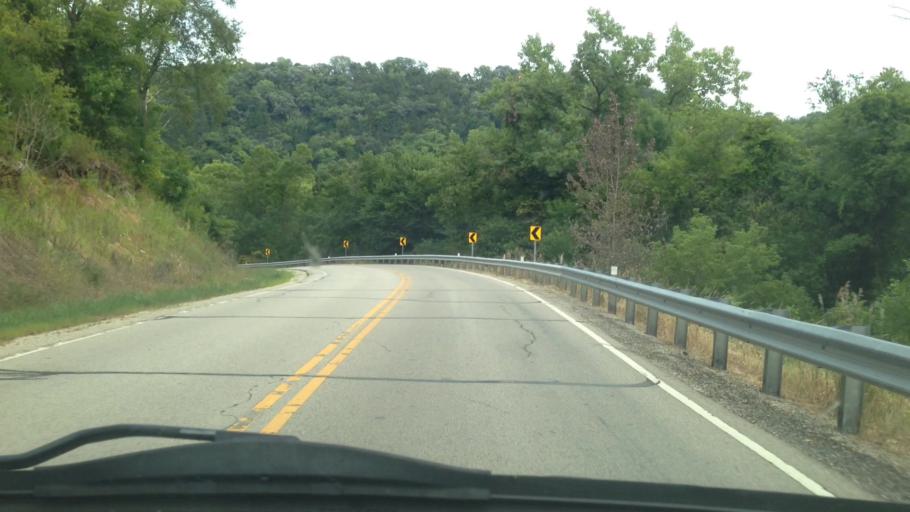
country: US
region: Minnesota
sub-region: Fillmore County
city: Preston
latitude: 43.7231
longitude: -91.9643
